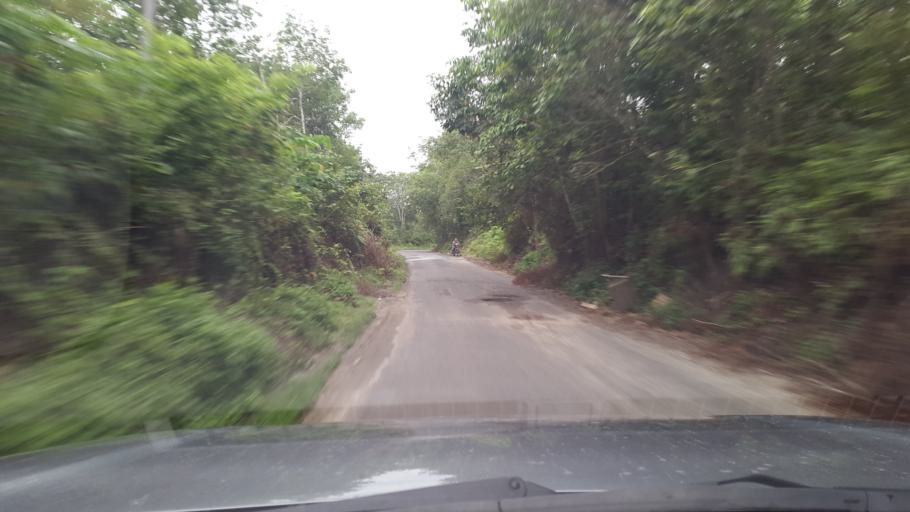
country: ID
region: South Sumatra
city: Gunungmenang
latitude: -3.1668
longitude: 103.9781
